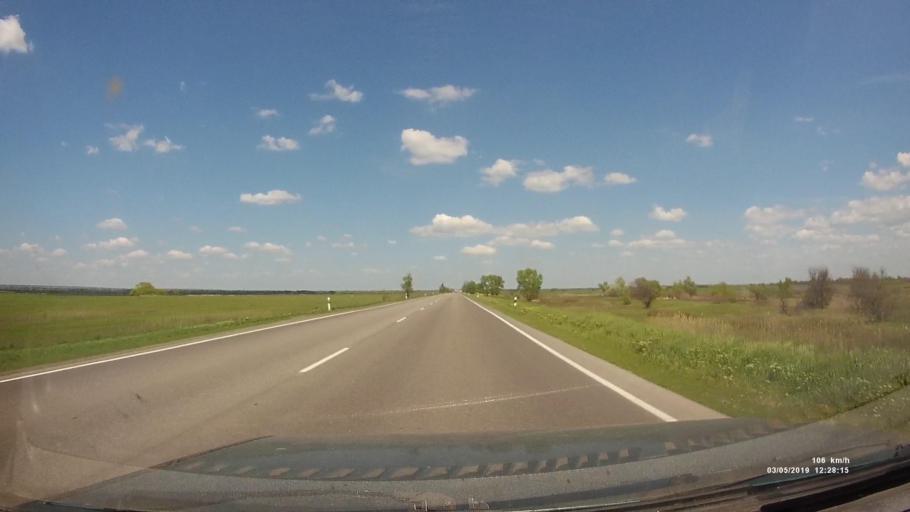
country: RU
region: Rostov
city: Semikarakorsk
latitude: 47.4705
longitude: 40.7270
